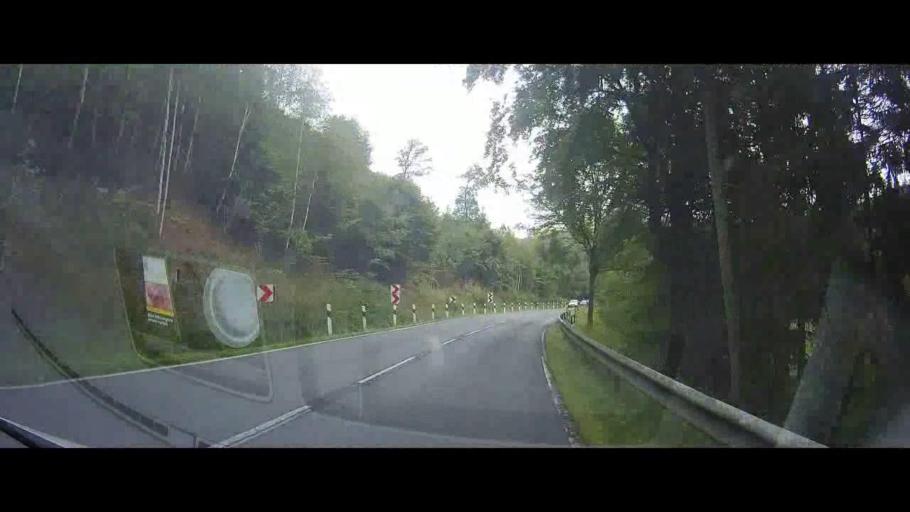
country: DE
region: Lower Saxony
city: Adelebsen
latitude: 51.5770
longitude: 9.7050
